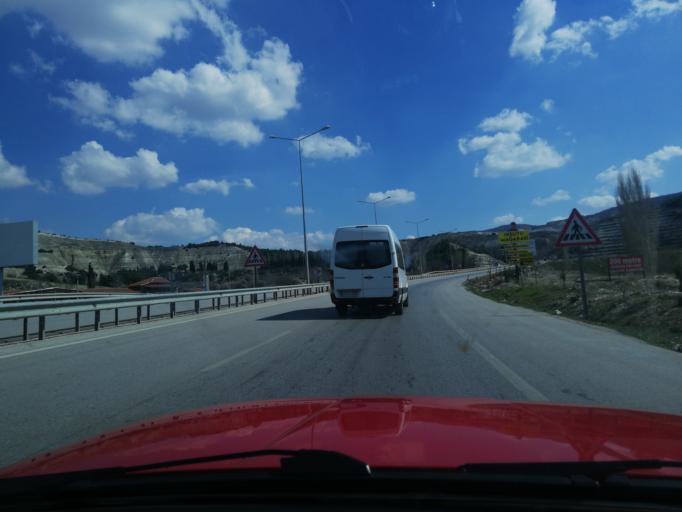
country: TR
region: Burdur
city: Burdur
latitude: 37.7074
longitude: 30.3052
